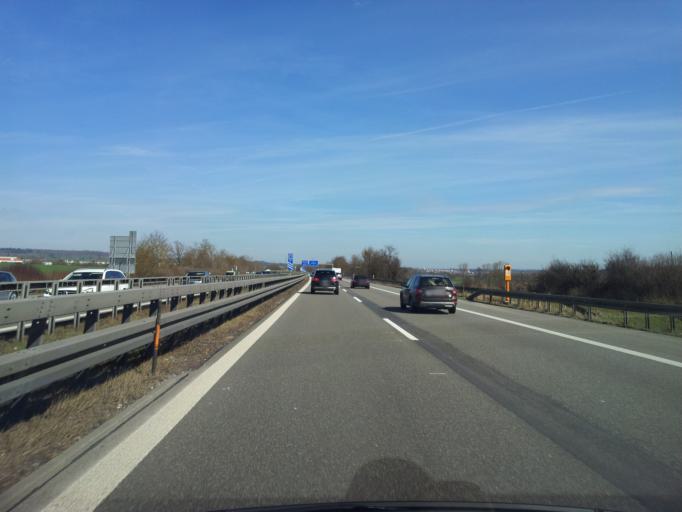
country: DE
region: Baden-Wuerttemberg
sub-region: Regierungsbezirk Stuttgart
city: Gartringen
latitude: 48.6256
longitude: 8.9132
